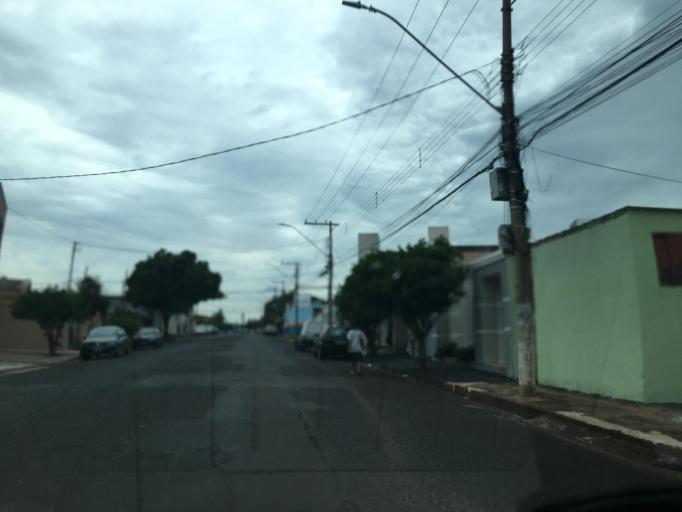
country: BR
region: Minas Gerais
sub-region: Uberlandia
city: Uberlandia
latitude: -18.9129
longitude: -48.3047
